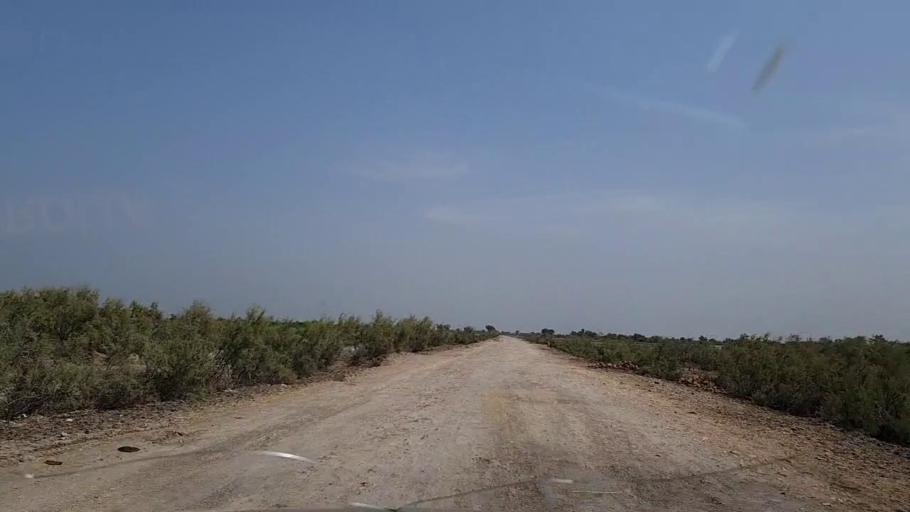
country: PK
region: Sindh
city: Khanpur
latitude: 27.8098
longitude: 69.3088
